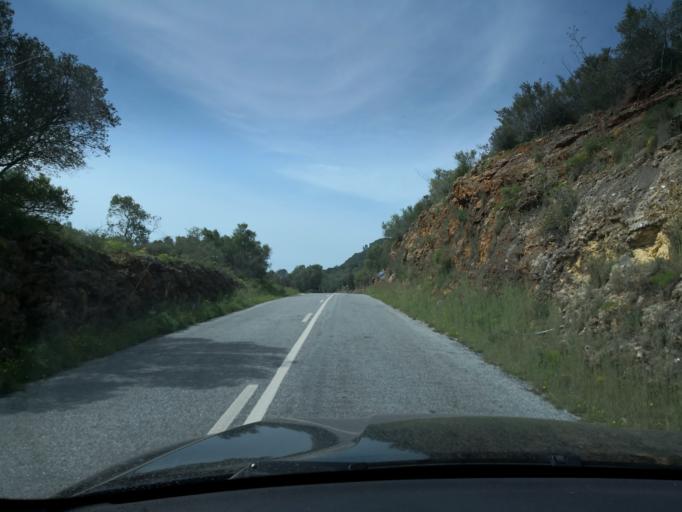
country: PT
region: Setubal
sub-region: Palmela
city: Quinta do Anjo
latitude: 38.4805
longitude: -8.9830
